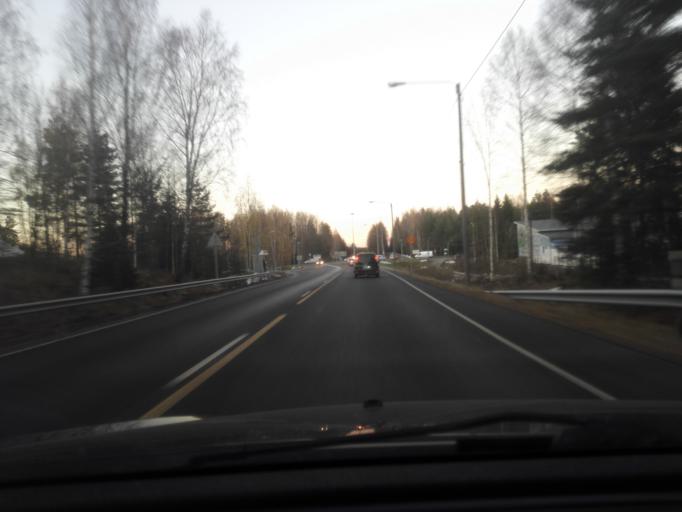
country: FI
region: Uusimaa
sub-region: Helsinki
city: Vantaa
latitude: 60.3034
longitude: 25.1043
